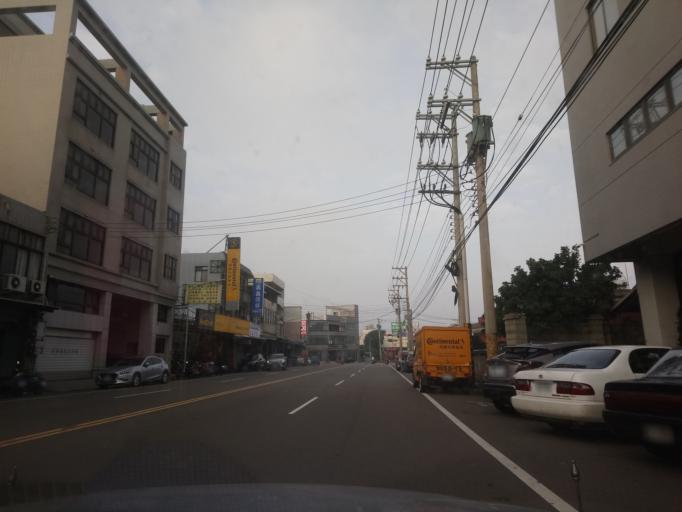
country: TW
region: Taiwan
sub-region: Hsinchu
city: Hsinchu
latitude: 24.7908
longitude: 120.9311
